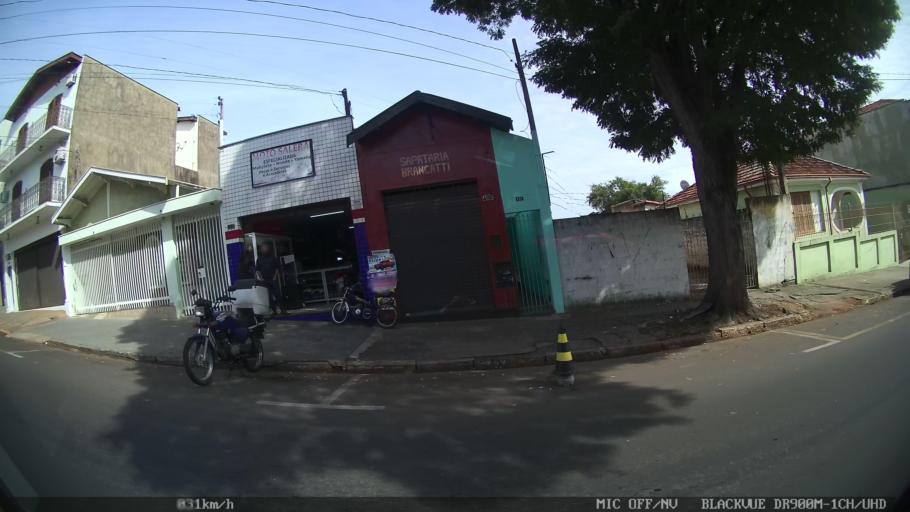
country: BR
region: Sao Paulo
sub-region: Piracicaba
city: Piracicaba
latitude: -22.7428
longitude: -47.6517
